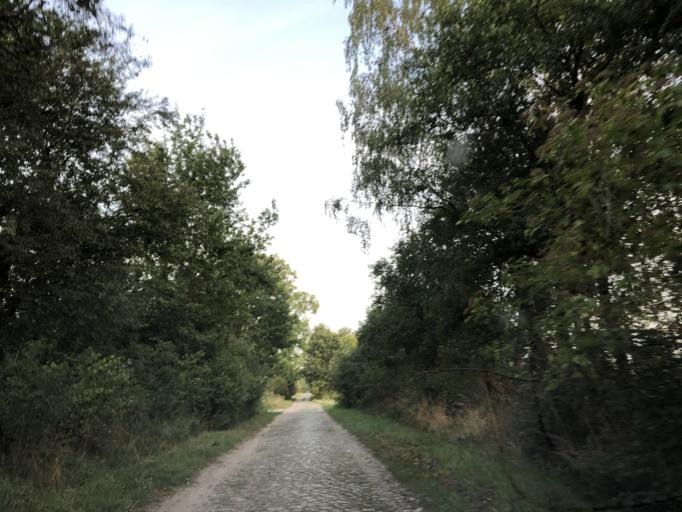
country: PL
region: Lubusz
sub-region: Powiat swiebodzinski
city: Zbaszynek
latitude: 52.2332
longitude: 15.7973
